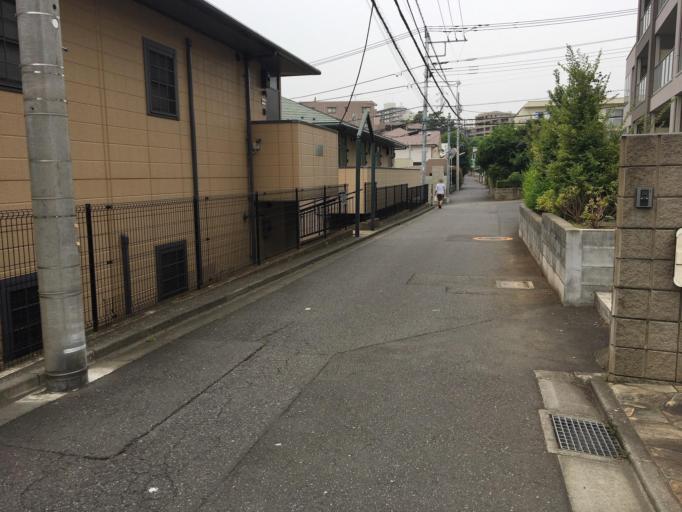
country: JP
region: Tokyo
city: Chofugaoka
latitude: 35.6591
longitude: 139.5701
